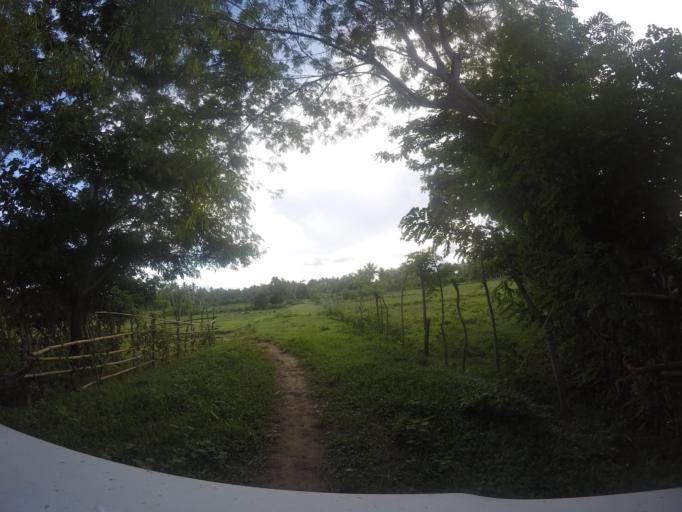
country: TL
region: Lautem
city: Lospalos
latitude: -8.5141
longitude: 126.9924
